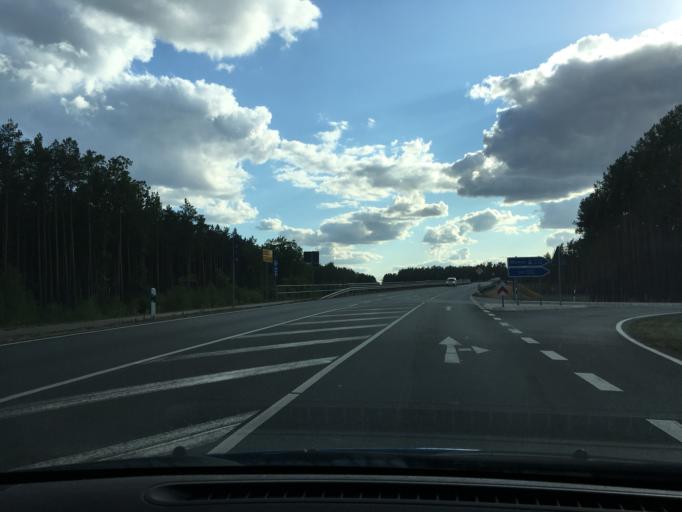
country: DE
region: Mecklenburg-Vorpommern
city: Gross Laasch
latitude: 53.3449
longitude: 11.5230
